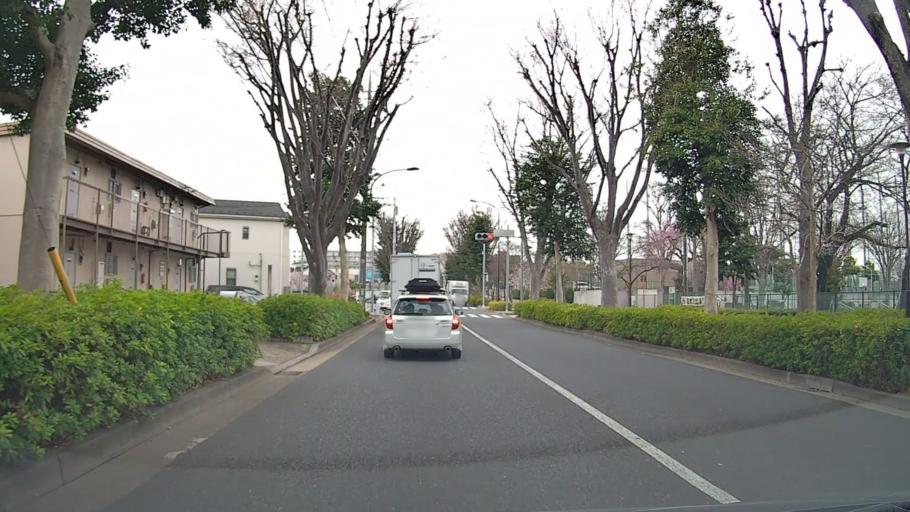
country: JP
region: Saitama
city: Asaka
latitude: 35.7764
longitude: 139.5905
